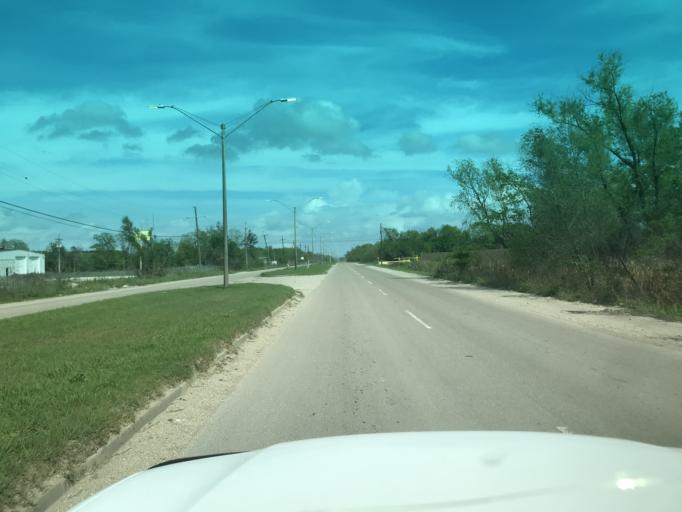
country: US
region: Louisiana
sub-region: Saint Bernard Parish
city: Arabi
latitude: 30.0095
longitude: -89.9778
